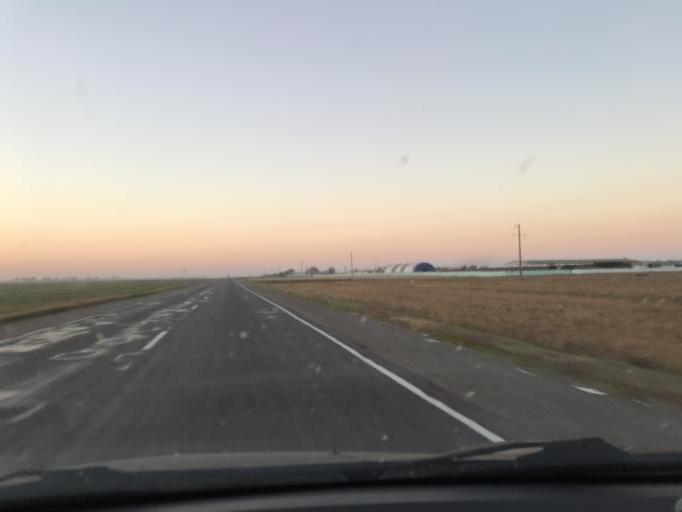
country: BY
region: Gomel
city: Horad Rechytsa
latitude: 52.2442
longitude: 30.5002
